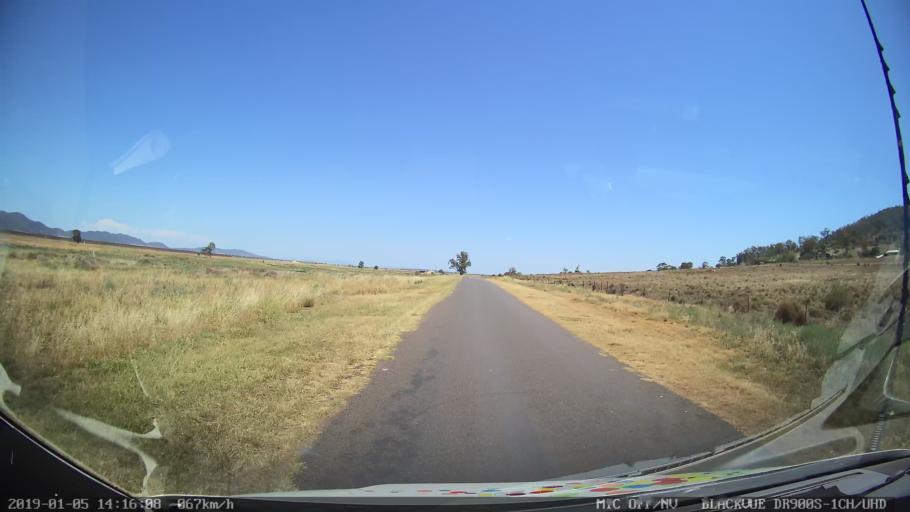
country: AU
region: New South Wales
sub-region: Liverpool Plains
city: Quirindi
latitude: -31.2538
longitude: 150.4724
